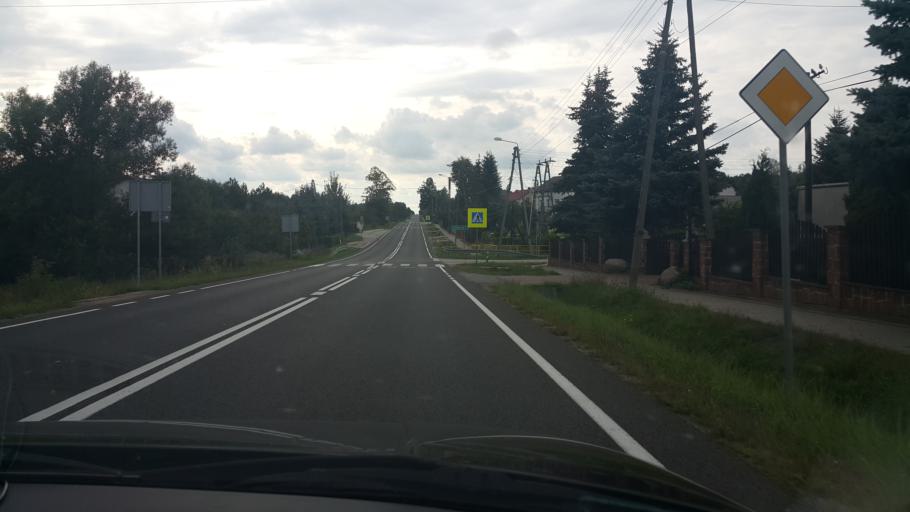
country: PL
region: Swietokrzyskie
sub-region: Powiat skarzyski
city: Blizyn
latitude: 51.0997
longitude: 20.7939
